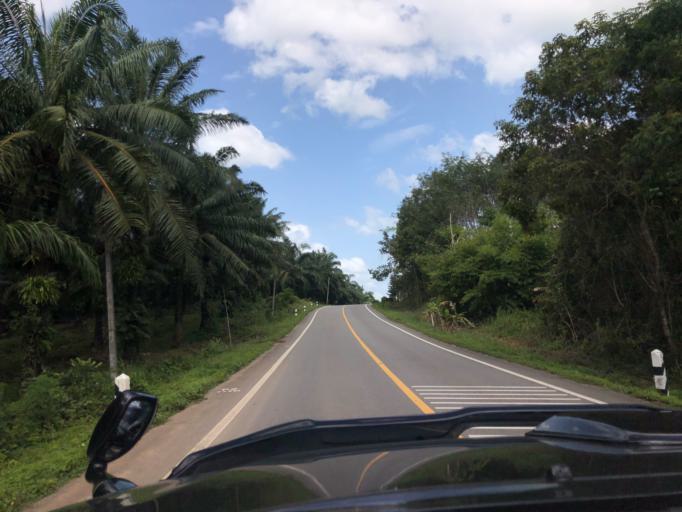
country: TH
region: Krabi
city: Khlong Thom
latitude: 7.9479
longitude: 99.2078
